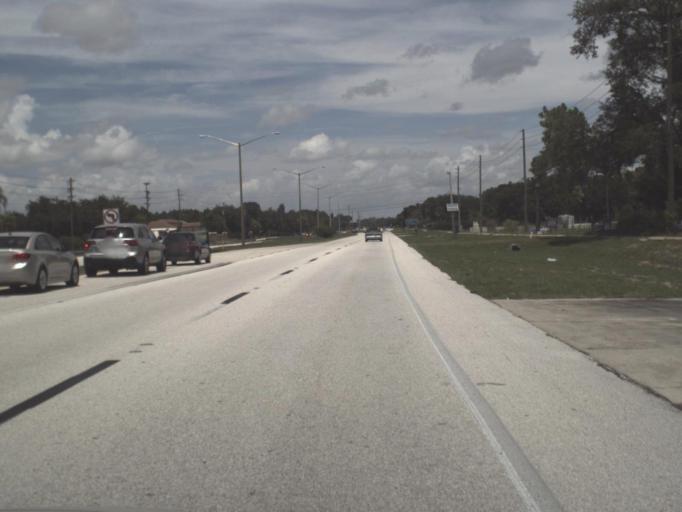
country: US
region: Florida
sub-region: Pinellas County
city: East Lake
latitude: 28.1307
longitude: -82.6971
